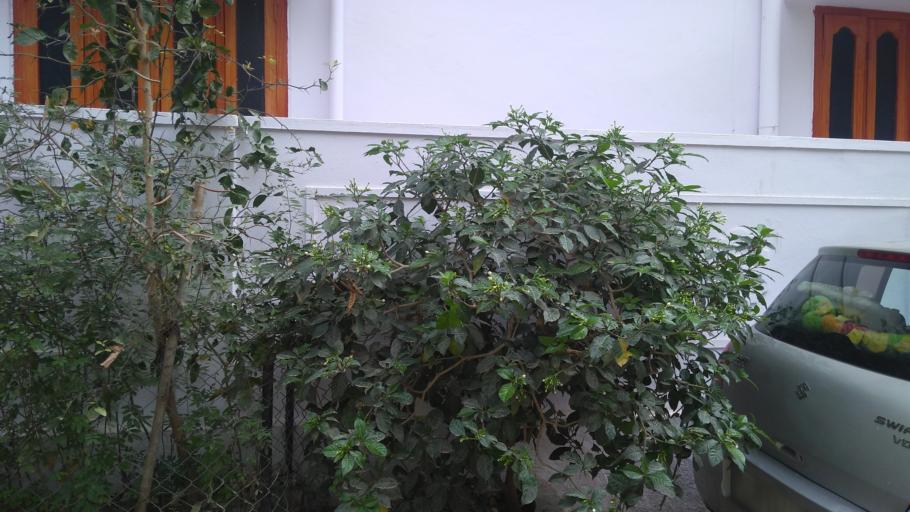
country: IN
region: Telangana
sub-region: Medak
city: Serilingampalle
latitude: 17.5146
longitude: 78.2983
